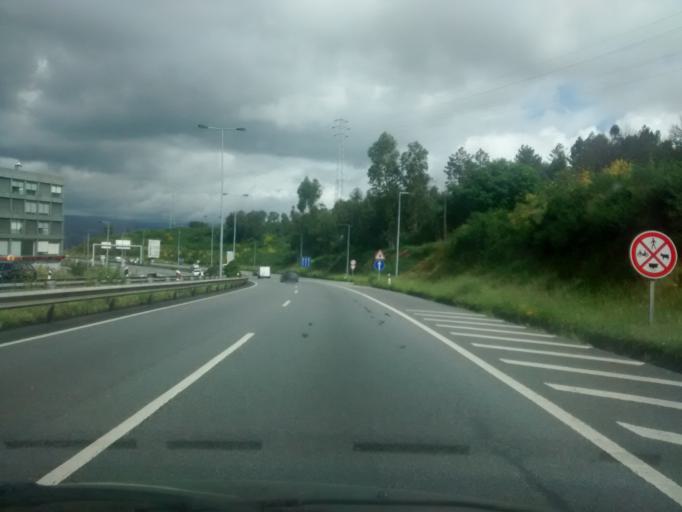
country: PT
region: Braga
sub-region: Braga
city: Braga
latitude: 41.5634
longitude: -8.4186
